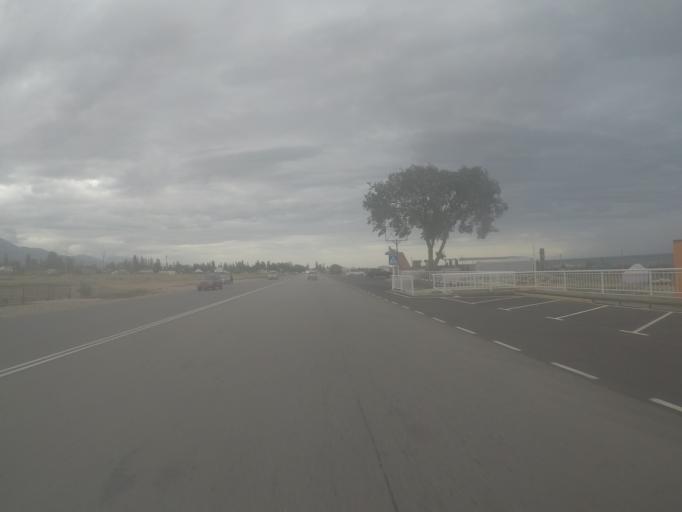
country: KG
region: Ysyk-Koel
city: Cholpon-Ata
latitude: 42.5973
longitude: 76.8500
